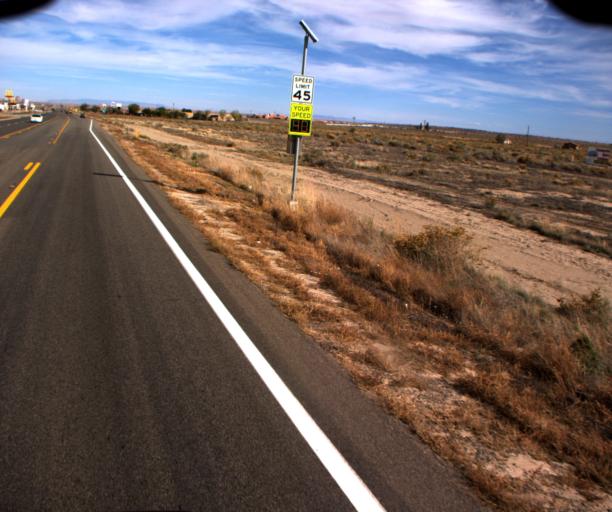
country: US
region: Arizona
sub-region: Navajo County
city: Kayenta
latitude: 36.7064
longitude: -110.2559
